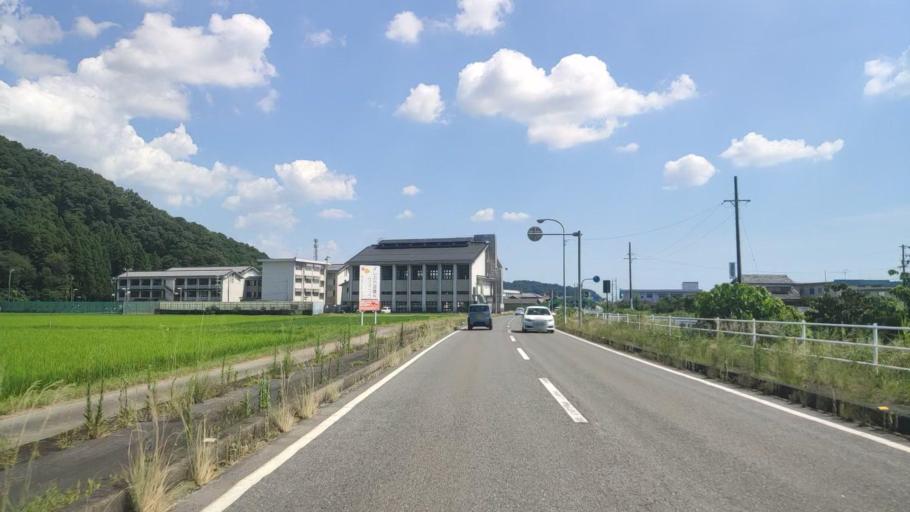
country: JP
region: Gifu
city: Godo
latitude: 35.4917
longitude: 136.6728
